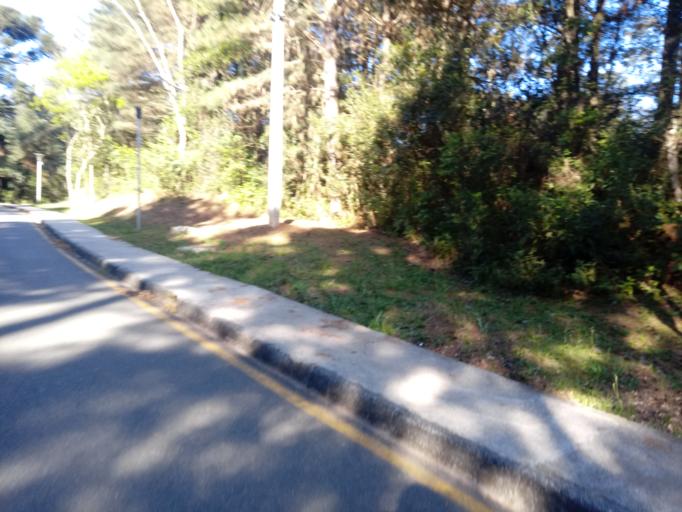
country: BR
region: Parana
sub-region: Curitiba
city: Curitiba
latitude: -25.4495
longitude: -49.2387
